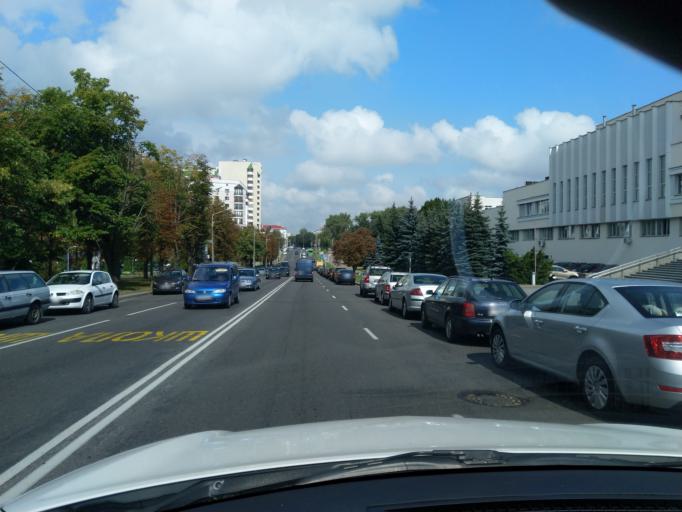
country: BY
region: Minsk
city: Minsk
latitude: 53.9003
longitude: 27.5849
